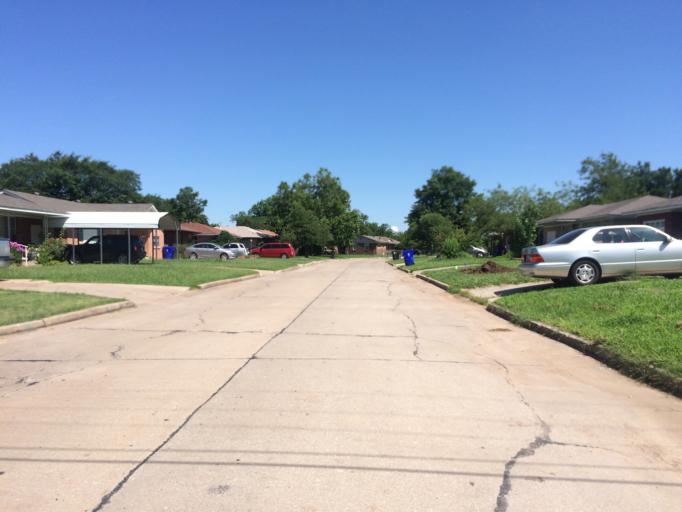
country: US
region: Oklahoma
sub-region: Cleveland County
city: Norman
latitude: 35.2306
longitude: -97.4567
